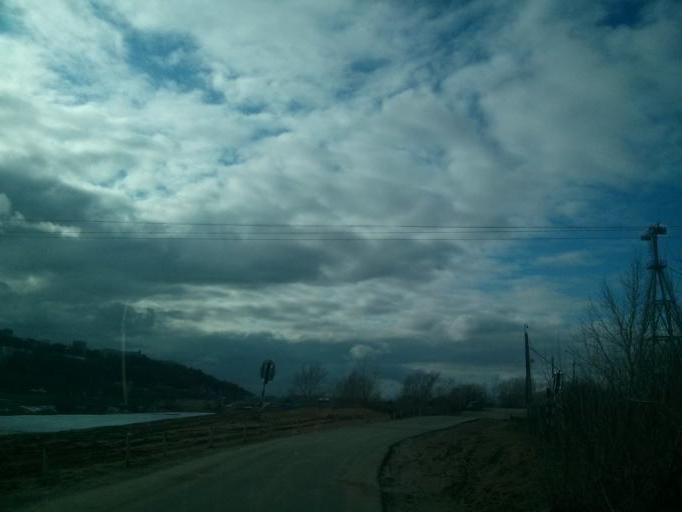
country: RU
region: Nizjnij Novgorod
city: Bor
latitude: 56.3290
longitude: 44.0454
